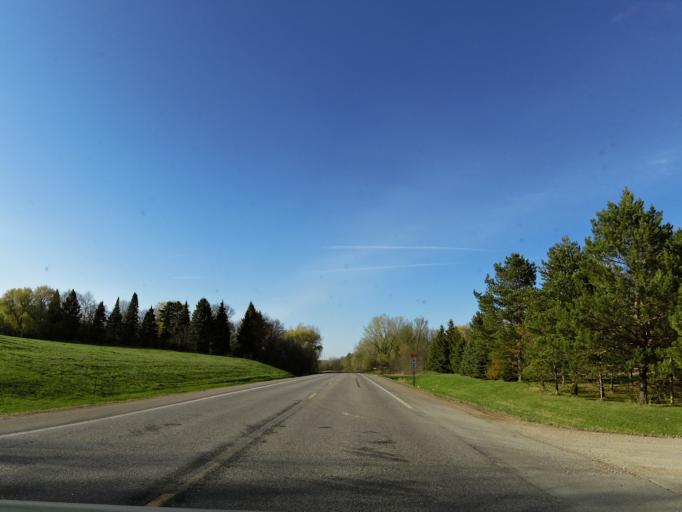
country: US
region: Minnesota
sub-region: Scott County
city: Elko New Market
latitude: 44.5735
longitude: -93.2847
